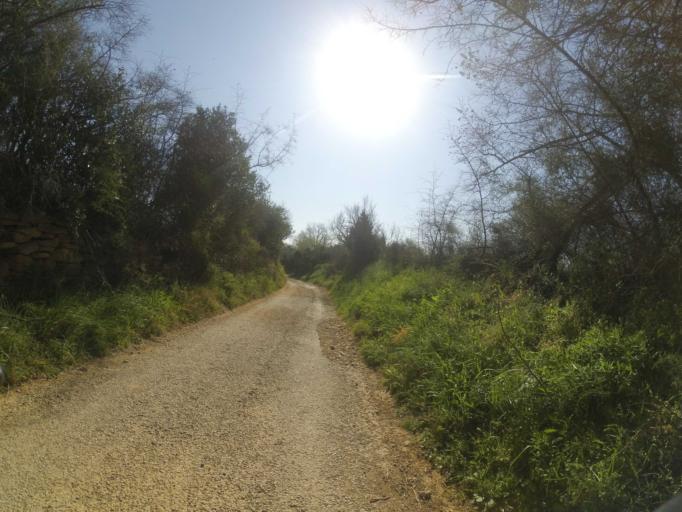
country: FR
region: Languedoc-Roussillon
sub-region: Departement des Pyrenees-Orientales
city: Llupia
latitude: 42.6189
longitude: 2.7636
